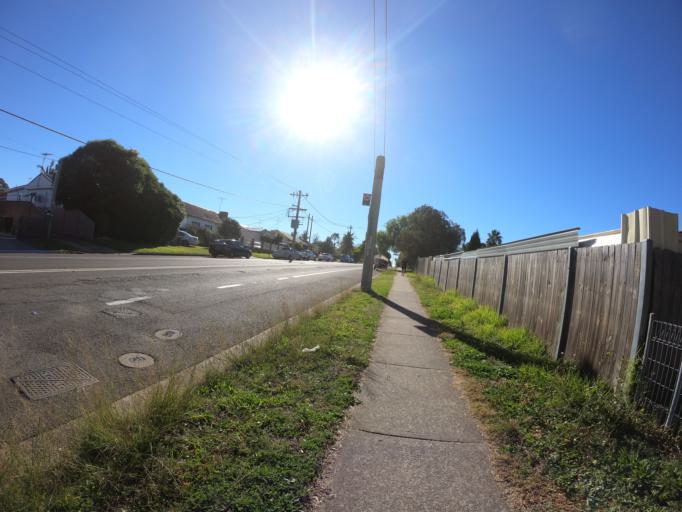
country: AU
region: New South Wales
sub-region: Hawkesbury
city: South Windsor
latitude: -33.6275
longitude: 150.7998
